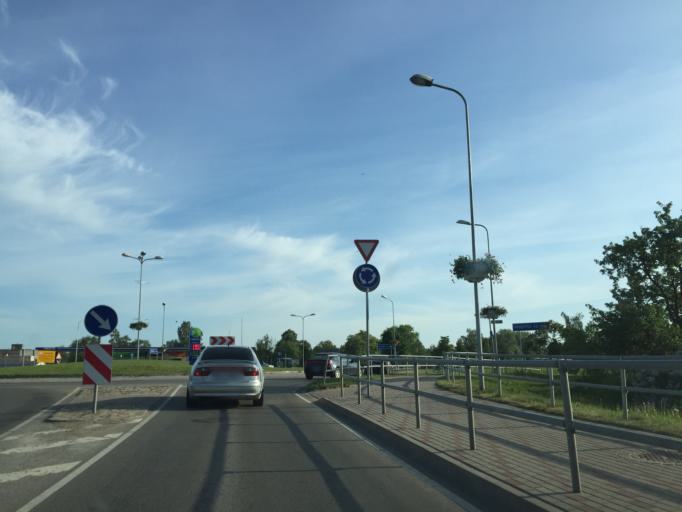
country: LV
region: Bauskas Rajons
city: Bauska
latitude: 56.4007
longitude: 24.1774
